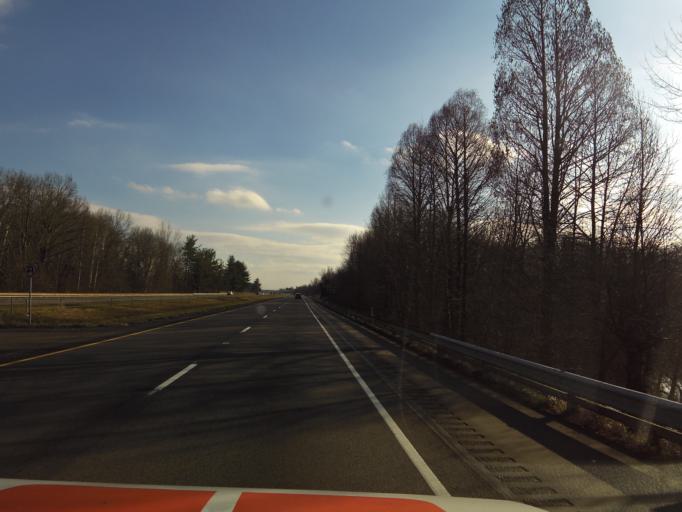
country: US
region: Indiana
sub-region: Scott County
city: Austin
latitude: 38.7503
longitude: -85.8237
